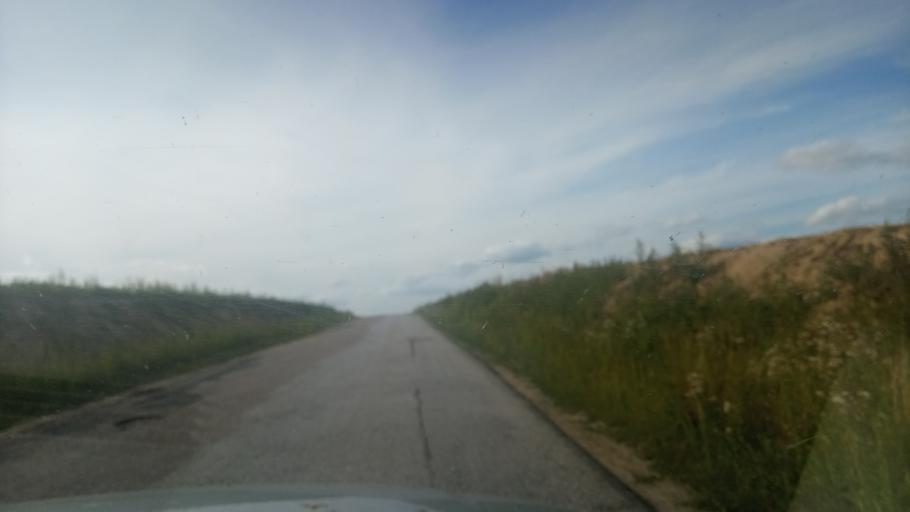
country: PL
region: Kujawsko-Pomorskie
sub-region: Powiat nakielski
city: Sadki
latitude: 53.1980
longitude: 17.3846
